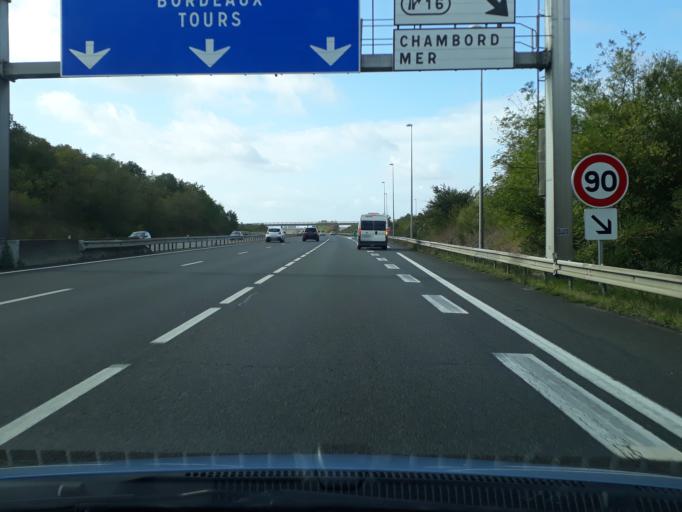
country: FR
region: Centre
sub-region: Departement du Loir-et-Cher
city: Mer
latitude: 47.7330
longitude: 1.5107
